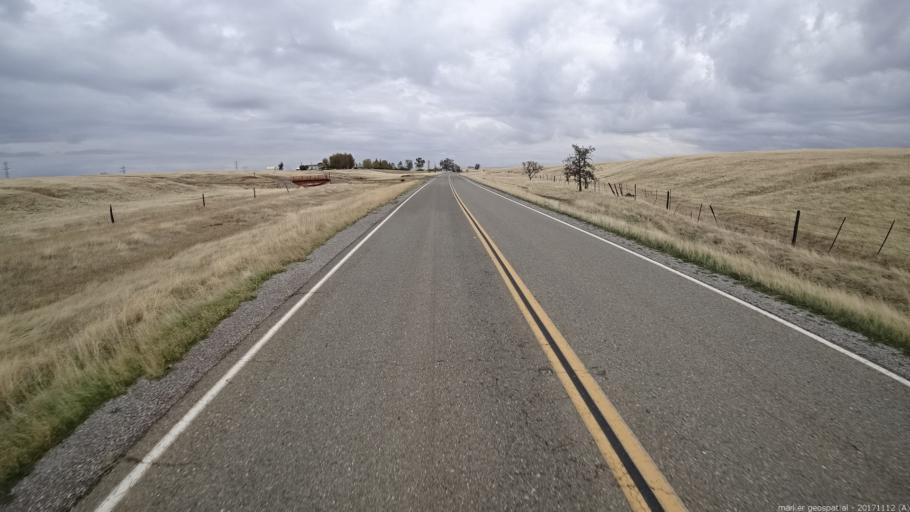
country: US
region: California
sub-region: Shasta County
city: Palo Cedro
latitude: 40.5102
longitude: -122.1891
